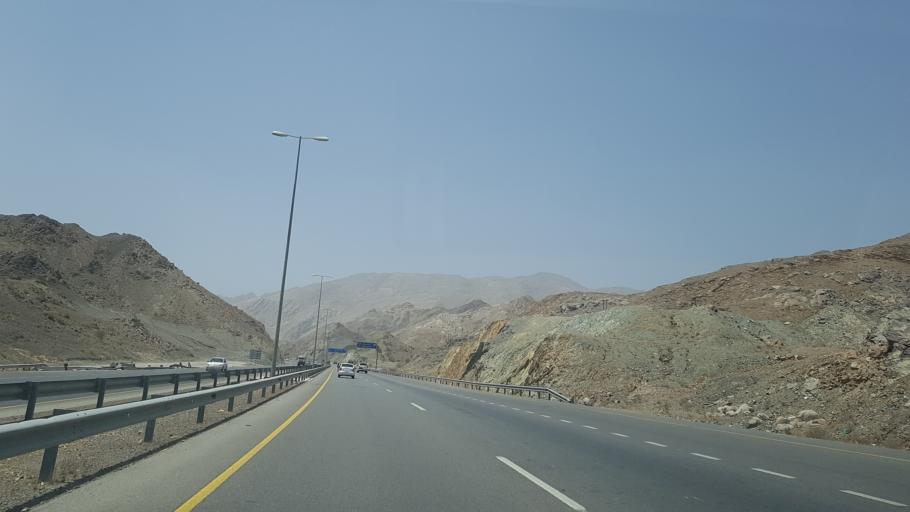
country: OM
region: Muhafazat ad Dakhiliyah
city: Bidbid
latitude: 23.4142
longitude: 58.0983
